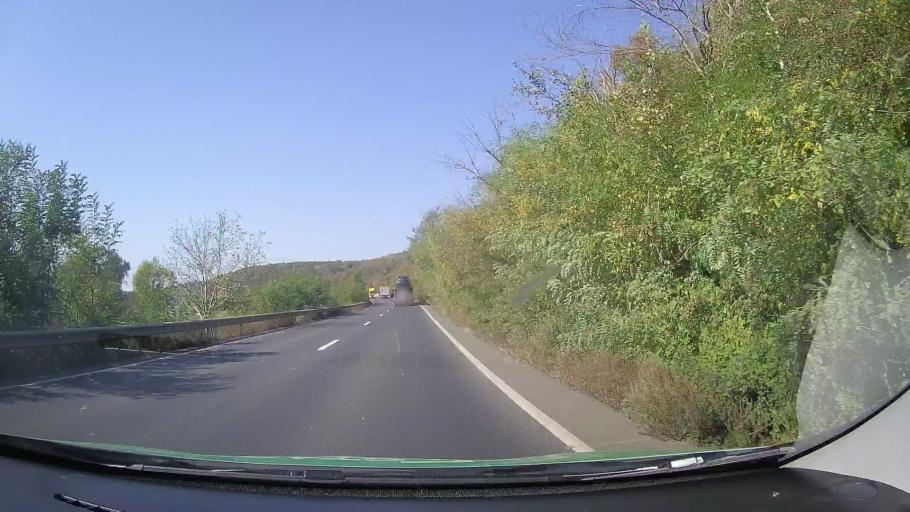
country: RO
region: Arad
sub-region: Comuna Bata
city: Bata
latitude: 46.0350
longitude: 22.0848
